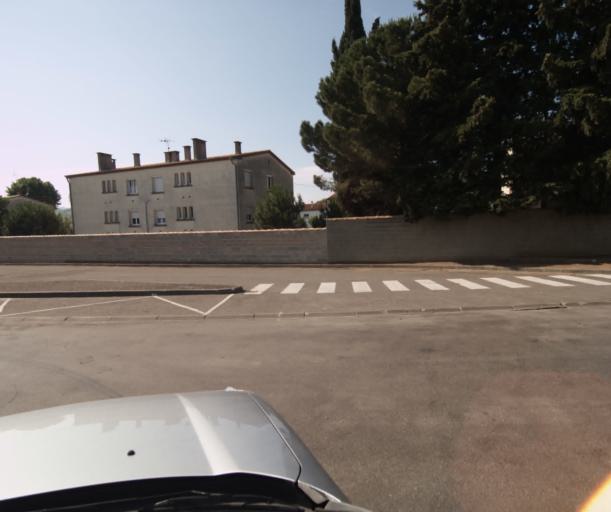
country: FR
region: Languedoc-Roussillon
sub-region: Departement de l'Aude
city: Limoux
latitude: 43.0684
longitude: 2.2167
